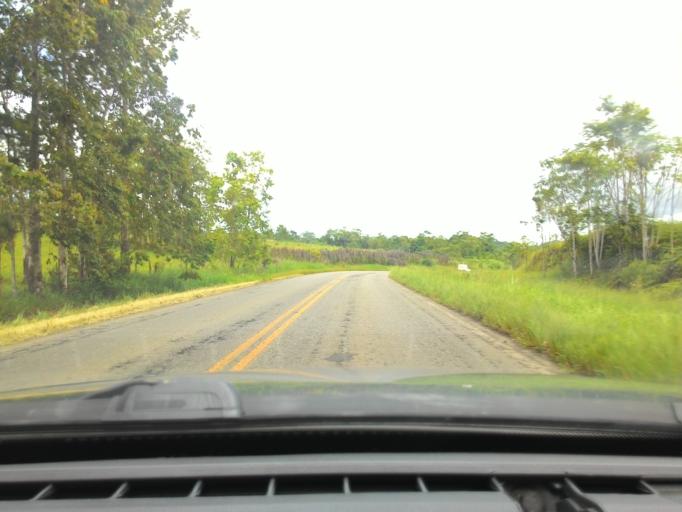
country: BR
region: Sao Paulo
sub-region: Pariquera-Acu
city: Pariquera Acu
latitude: -24.7397
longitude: -47.8100
